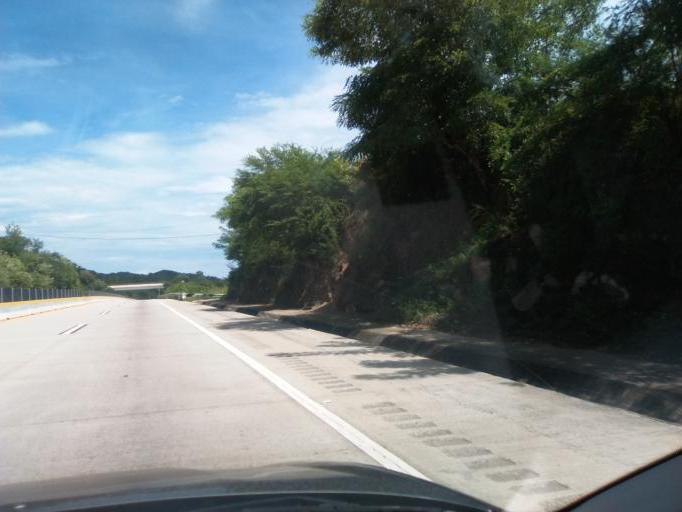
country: MX
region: Guerrero
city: Xaltianguis
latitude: 17.0236
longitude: -99.6530
